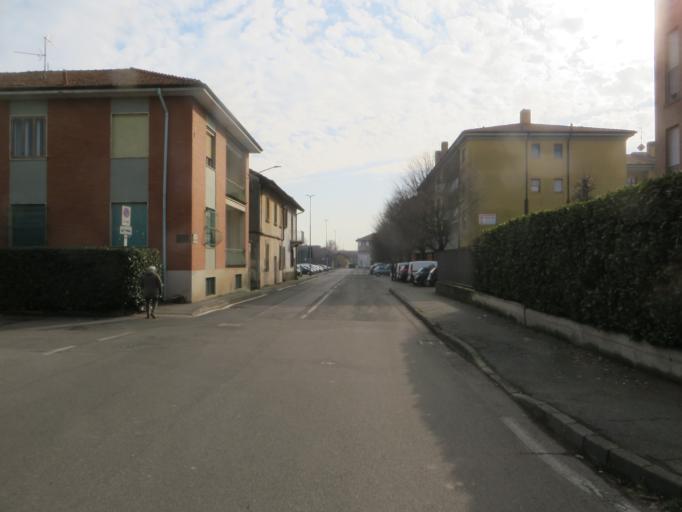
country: IT
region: Lombardy
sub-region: Citta metropolitana di Milano
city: Cornaredo
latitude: 45.4896
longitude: 9.0106
